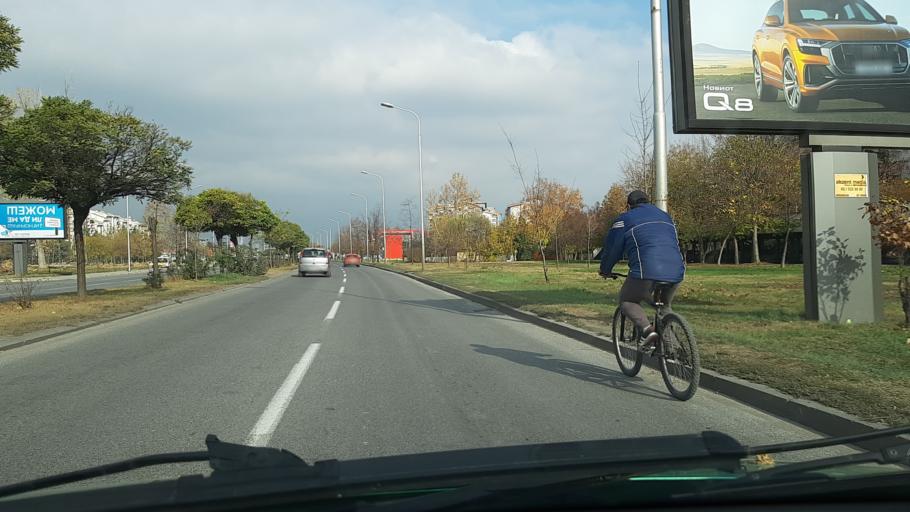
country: MK
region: Kisela Voda
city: Usje
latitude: 41.9842
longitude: 21.4723
